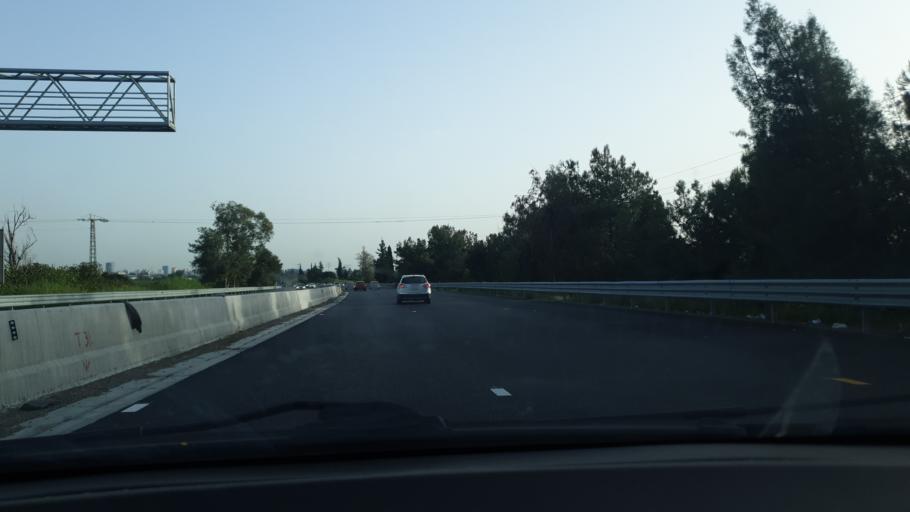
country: IL
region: Central District
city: Tel Mond
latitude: 32.2274
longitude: 34.8830
